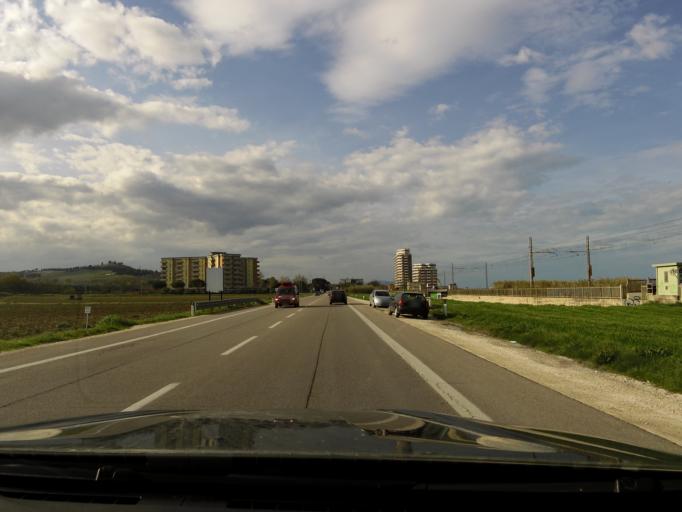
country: IT
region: The Marches
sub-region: Provincia di Macerata
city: Porto Potenza Picena
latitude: 43.3452
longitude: 13.7042
